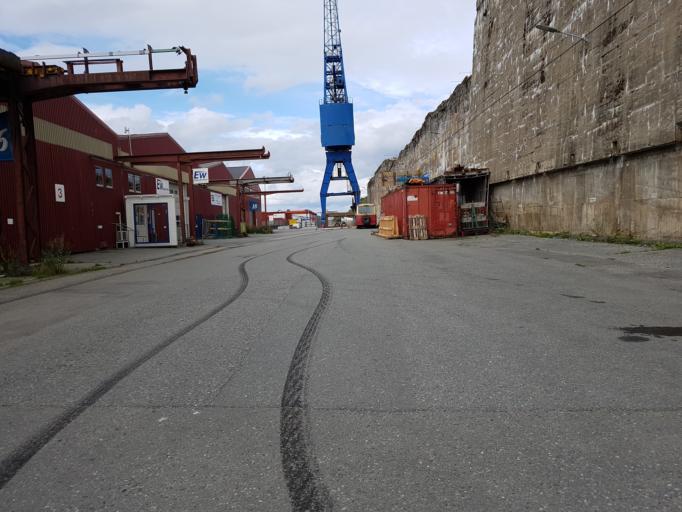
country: NO
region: Sor-Trondelag
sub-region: Trondheim
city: Trondheim
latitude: 63.4407
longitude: 10.4160
